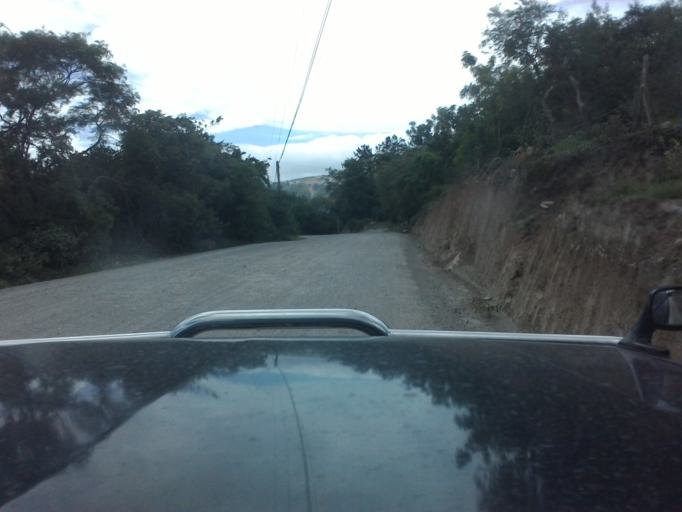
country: CR
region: Guanacaste
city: Juntas
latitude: 10.2807
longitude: -84.8426
